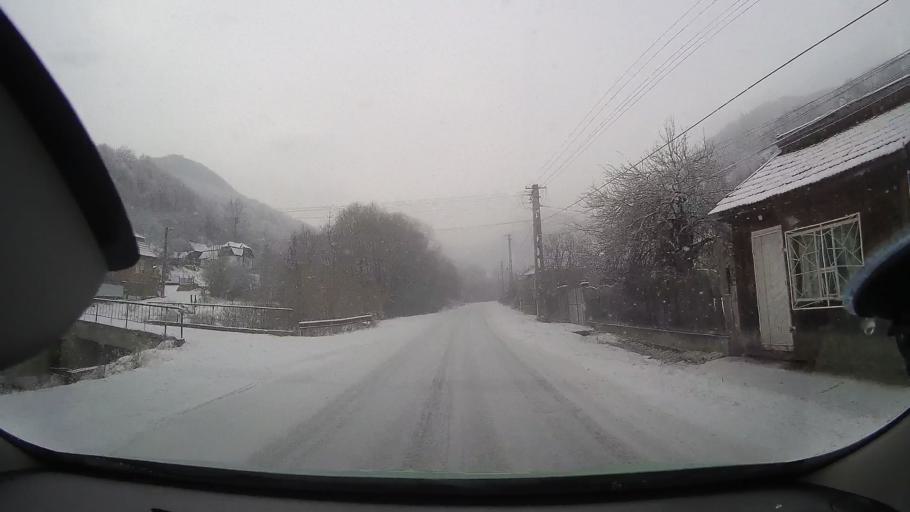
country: RO
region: Cluj
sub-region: Comuna Moldovenesti
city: Moldovenesti
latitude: 46.5045
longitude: 23.5997
